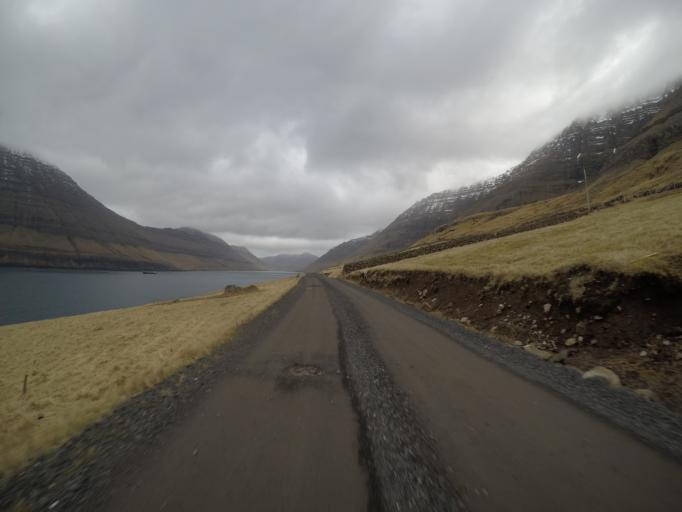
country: FO
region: Nordoyar
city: Klaksvik
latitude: 62.3487
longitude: -6.5819
